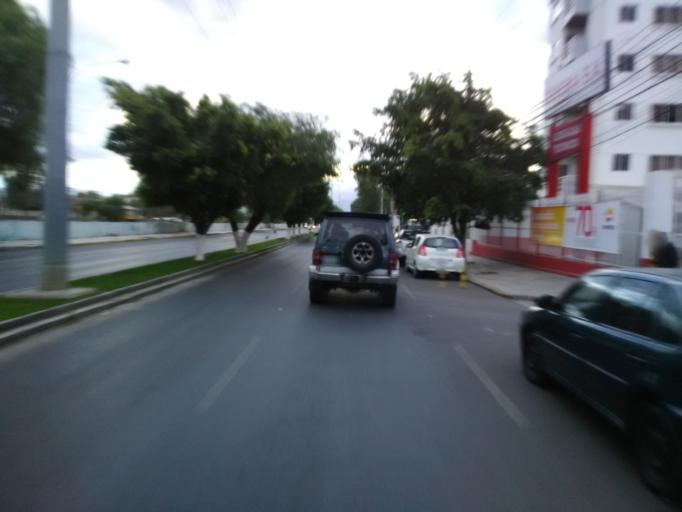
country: BO
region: Cochabamba
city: Cochabamba
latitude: -17.3772
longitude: -66.1441
